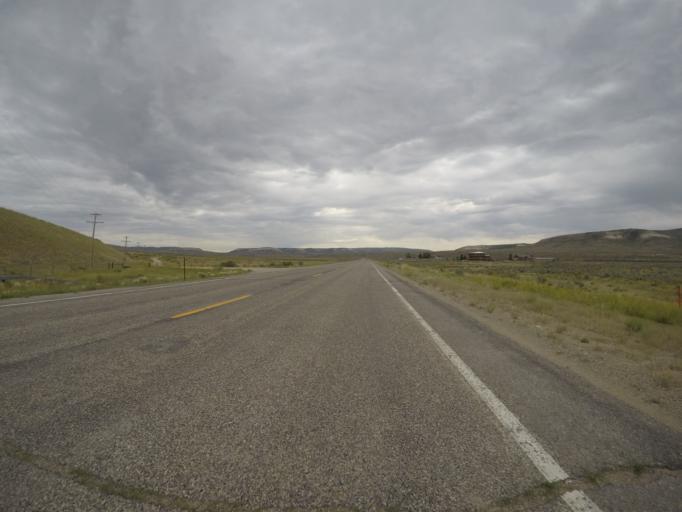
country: US
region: Wyoming
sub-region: Lincoln County
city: Kemmerer
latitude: 41.8205
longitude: -110.7292
